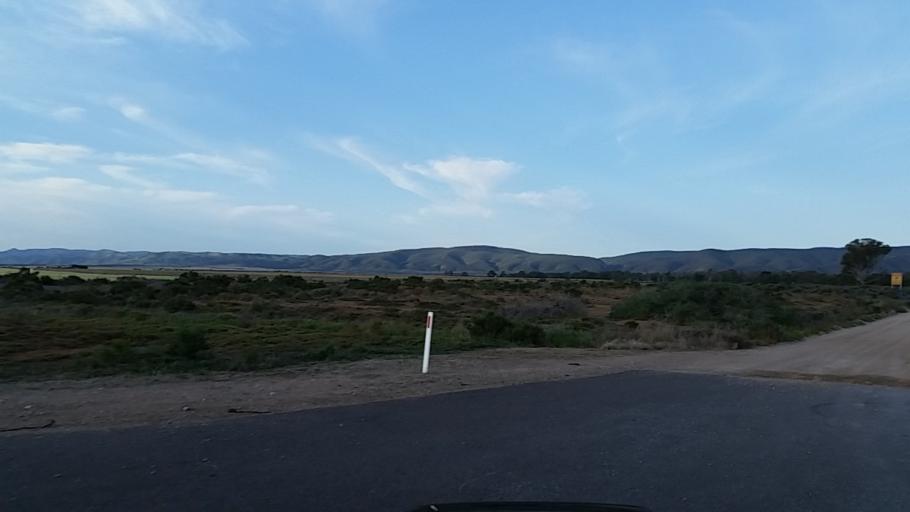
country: AU
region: South Australia
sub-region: Port Pirie City and Dists
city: Port Pirie
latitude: -33.0676
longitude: 138.0412
